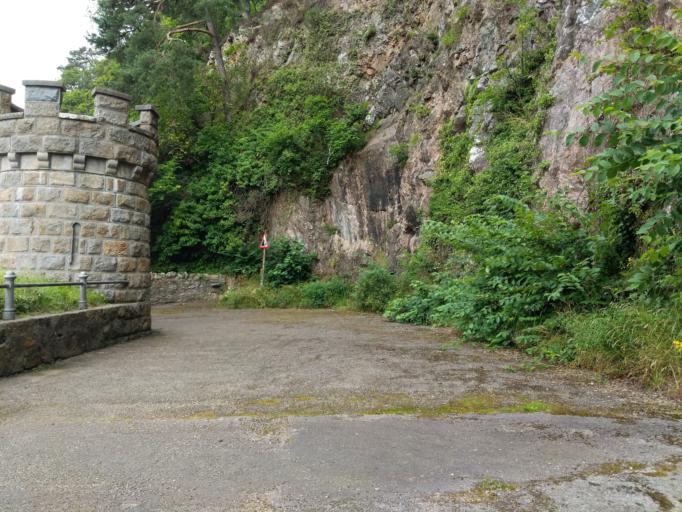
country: GB
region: Scotland
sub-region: Moray
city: Rothes
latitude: 57.4917
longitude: -3.1937
